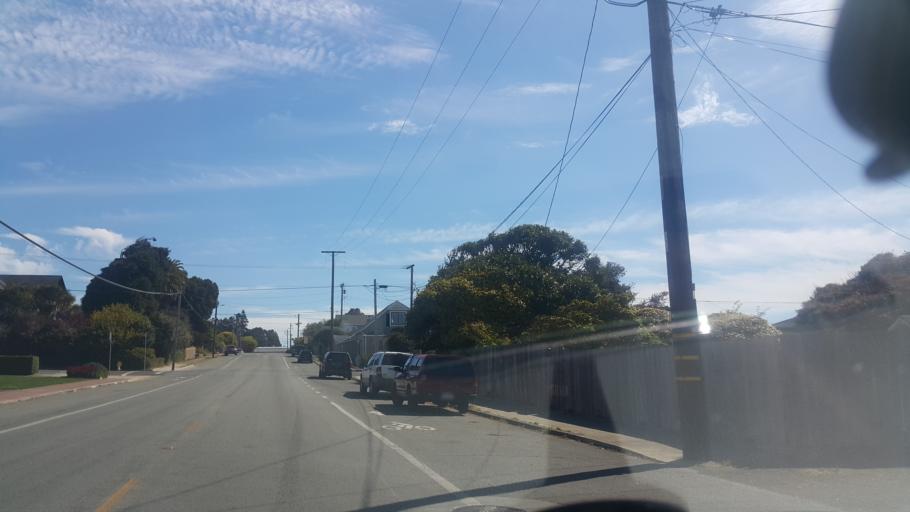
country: US
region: California
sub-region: Mendocino County
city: Fort Bragg
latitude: 39.4480
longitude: -123.8015
